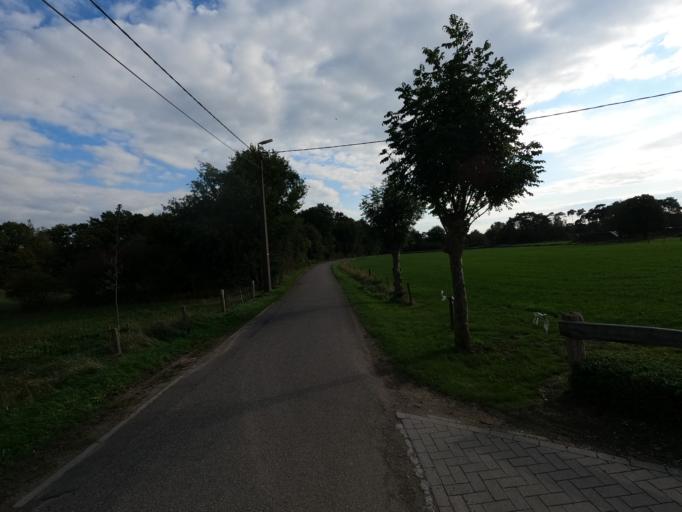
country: BE
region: Flanders
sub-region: Provincie Antwerpen
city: Vorselaar
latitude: 51.1892
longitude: 4.7839
